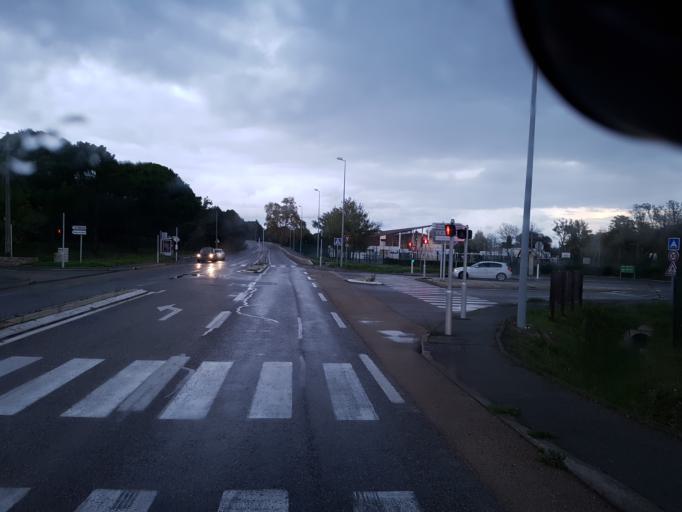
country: FR
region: Provence-Alpes-Cote d'Azur
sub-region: Departement du Var
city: Gassin
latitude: 43.2448
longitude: 6.5710
